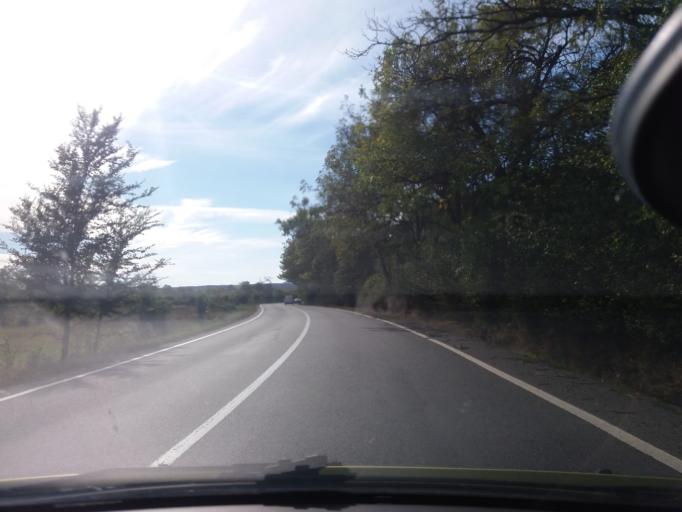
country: RO
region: Hunedoara
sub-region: Comuna Dobra
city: Dobra
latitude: 45.9399
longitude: 22.5334
